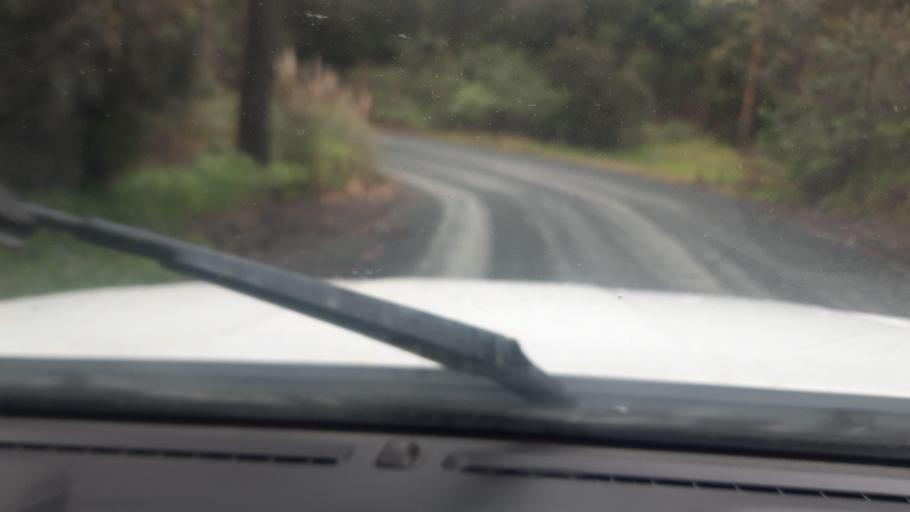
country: NZ
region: Northland
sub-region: Far North District
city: Kaitaia
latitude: -35.0016
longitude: 173.2150
